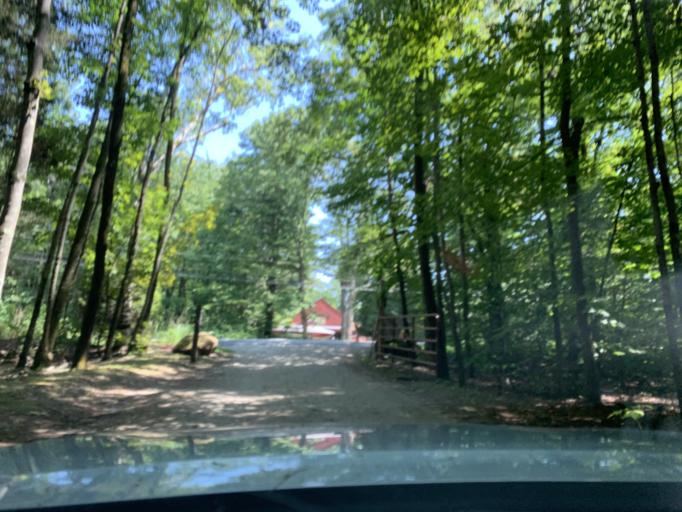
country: US
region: Massachusetts
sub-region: Berkshire County
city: Becket
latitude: 42.3009
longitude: -73.0619
